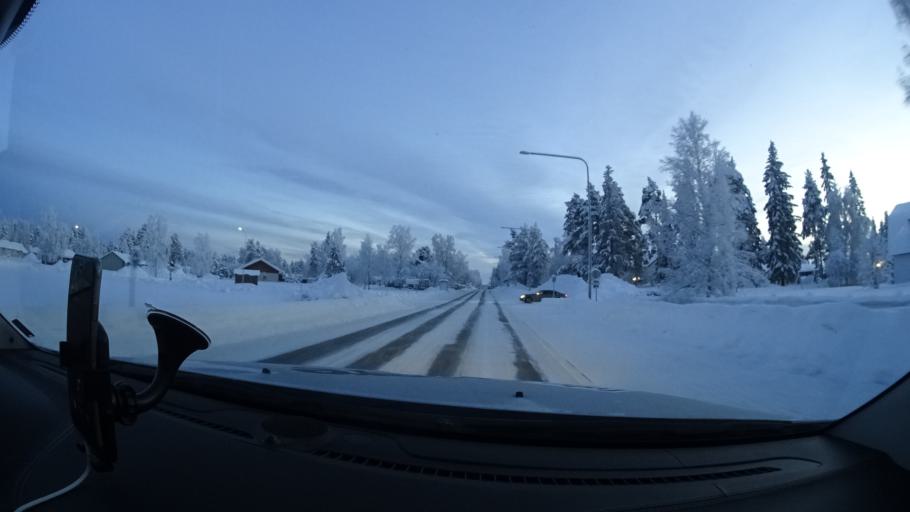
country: SE
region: Vaesterbotten
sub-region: Norsjo Kommun
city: Norsjoe
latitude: 64.9178
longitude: 19.4722
